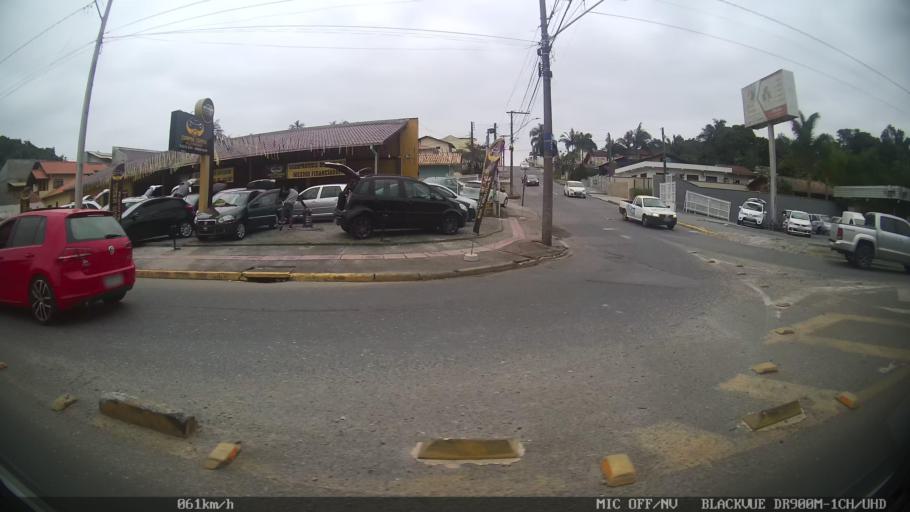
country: BR
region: Santa Catarina
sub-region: Joinville
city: Joinville
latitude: -26.3436
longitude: -48.8431
